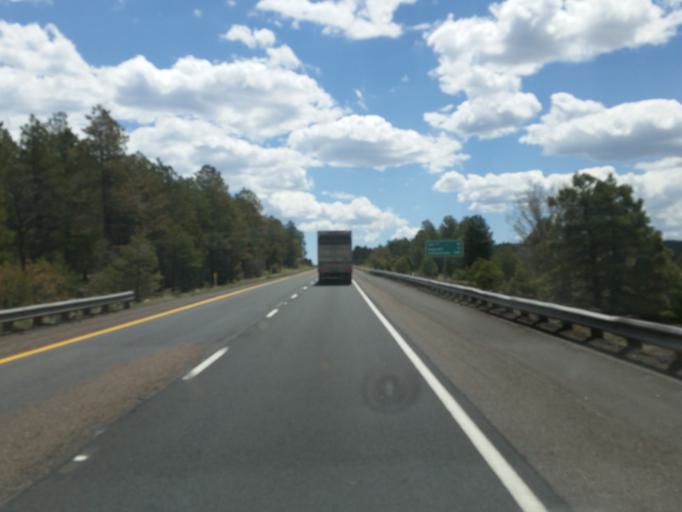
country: US
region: Arizona
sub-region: Coconino County
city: Parks
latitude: 35.2543
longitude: -111.9169
